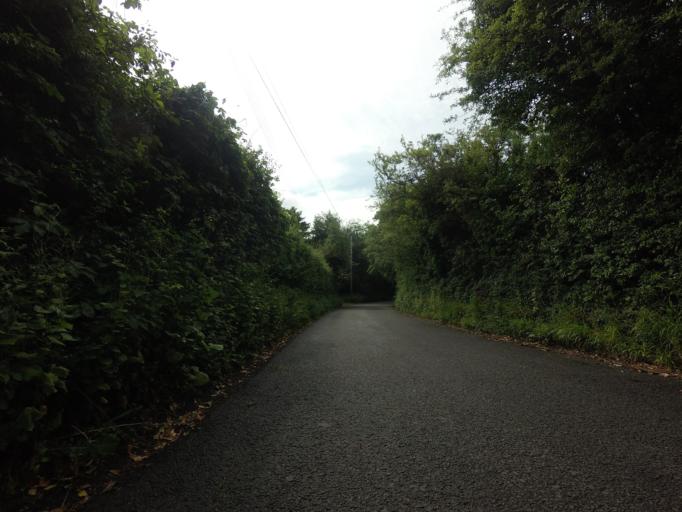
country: GB
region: England
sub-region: Kent
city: Halstead
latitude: 51.3537
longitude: 0.1382
